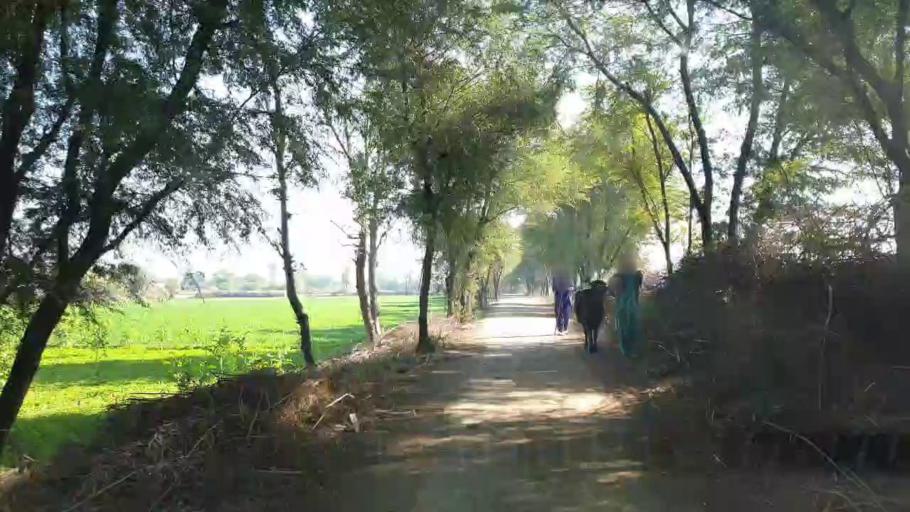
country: PK
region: Sindh
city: Shahpur Chakar
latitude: 26.0609
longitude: 68.4803
